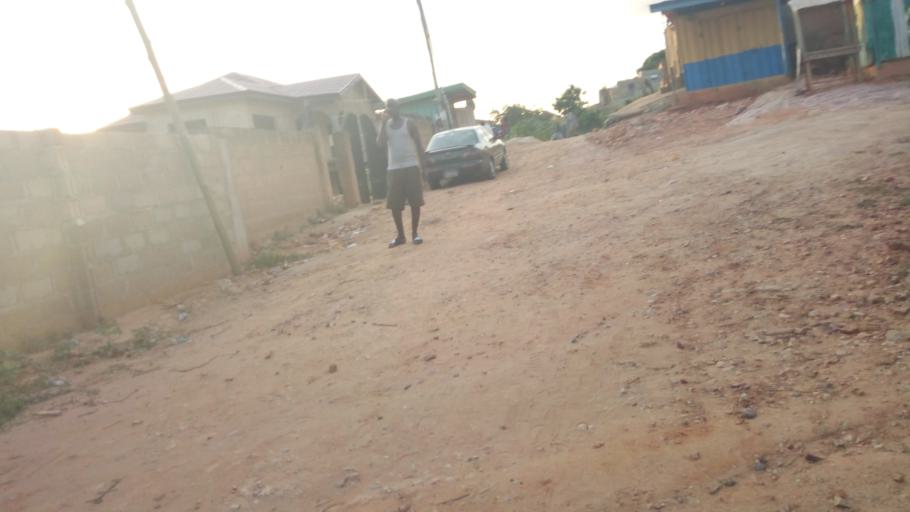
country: GH
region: Greater Accra
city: Gbawe
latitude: 5.5606
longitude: -0.3054
